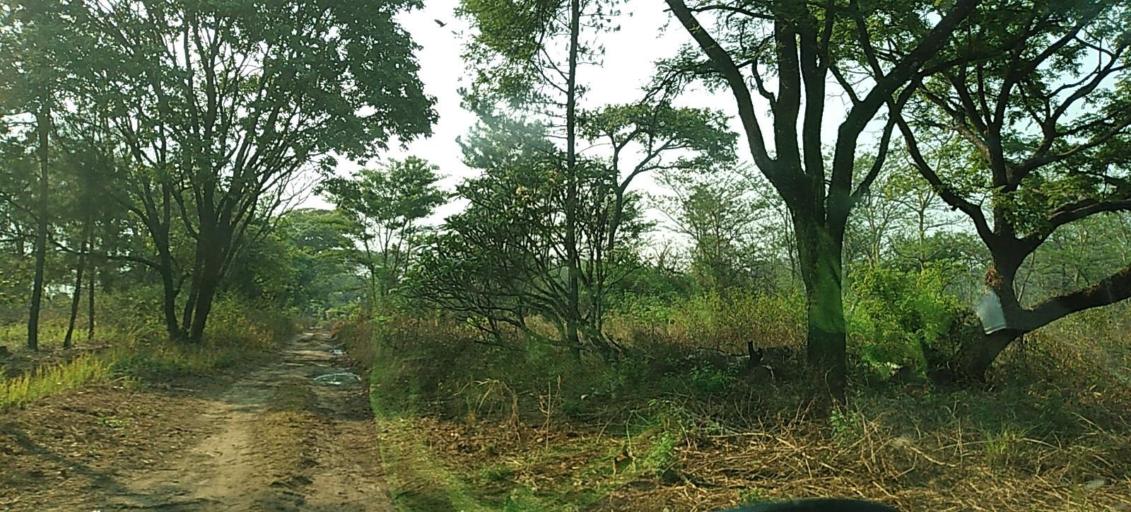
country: ZM
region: North-Western
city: Solwezi
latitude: -12.3906
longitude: 26.5741
